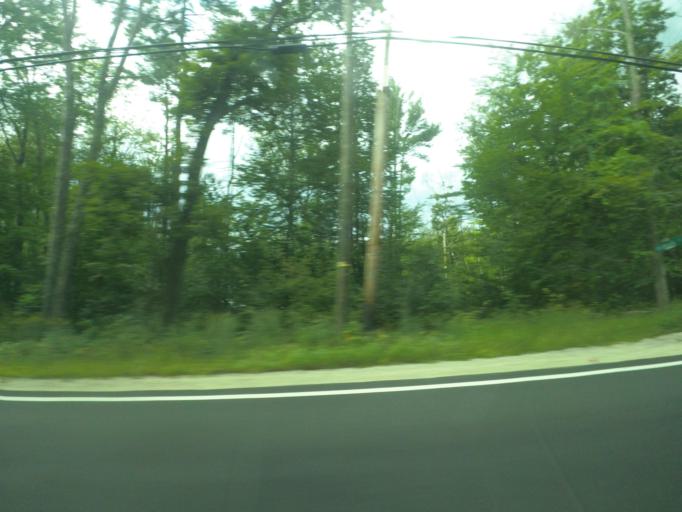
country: US
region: New Hampshire
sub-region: Strafford County
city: Barrington
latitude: 43.2156
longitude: -71.0802
